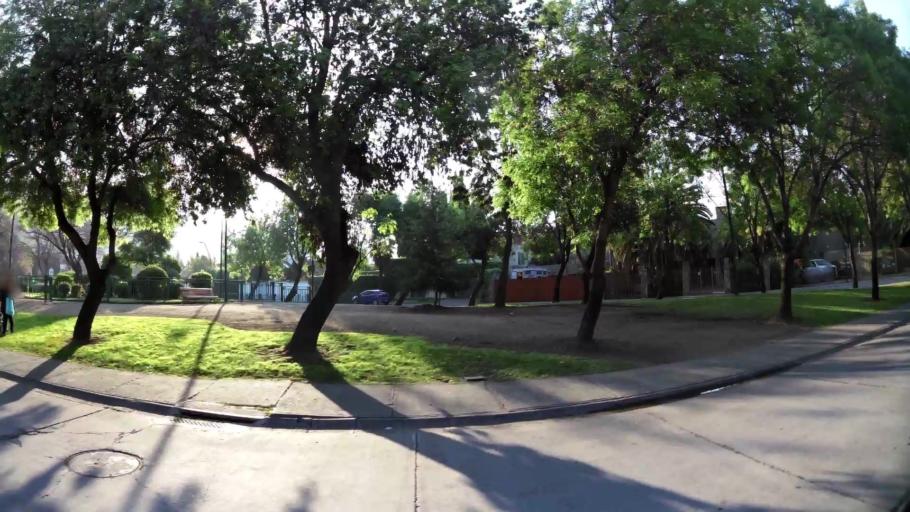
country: CL
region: Santiago Metropolitan
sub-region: Provincia de Santiago
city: Villa Presidente Frei, Nunoa, Santiago, Chile
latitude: -33.3469
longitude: -70.5464
